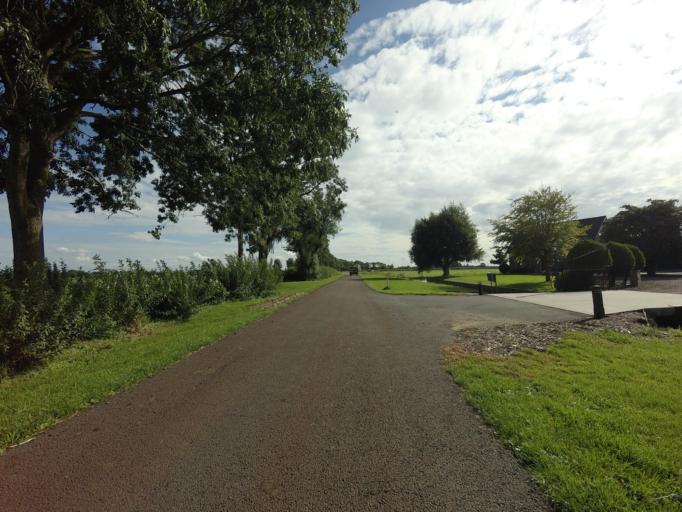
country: NL
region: Utrecht
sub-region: Stichtse Vecht
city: Breukelen
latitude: 52.2129
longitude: 4.9700
